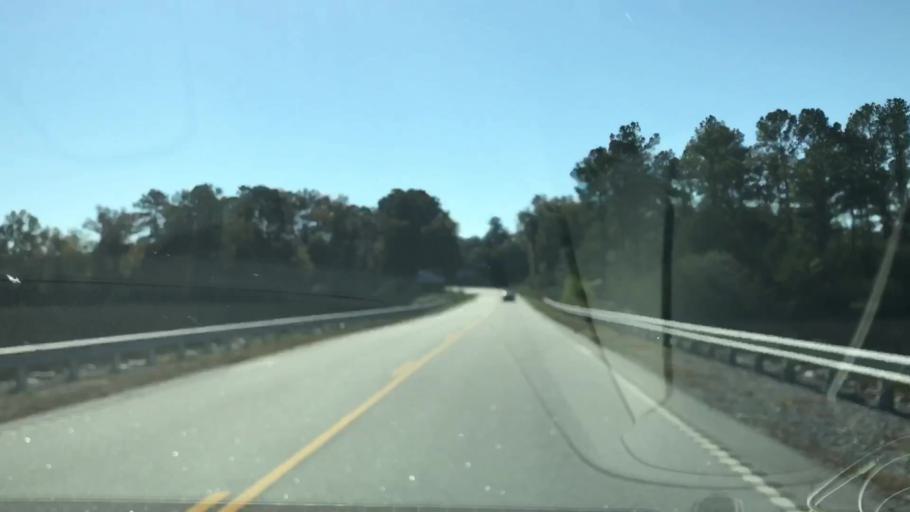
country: US
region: South Carolina
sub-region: Jasper County
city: Ridgeland
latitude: 32.5430
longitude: -80.9123
